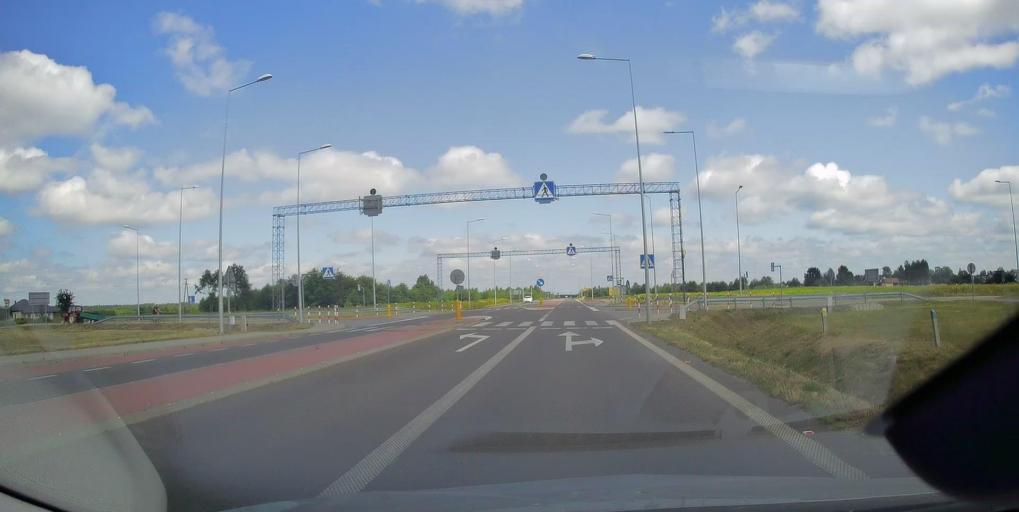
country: PL
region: Subcarpathian Voivodeship
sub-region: Powiat mielecki
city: Mielec
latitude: 50.3291
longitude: 21.4865
